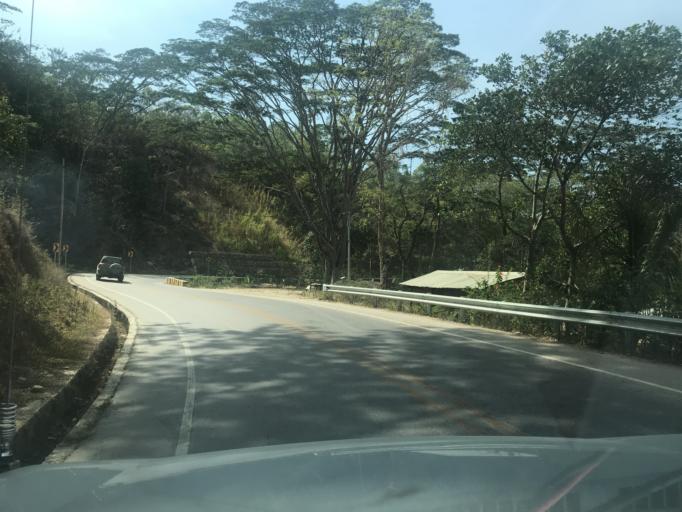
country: TL
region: Aileu
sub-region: Aileu Villa
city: Aileu
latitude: -8.6785
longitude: 125.5509
